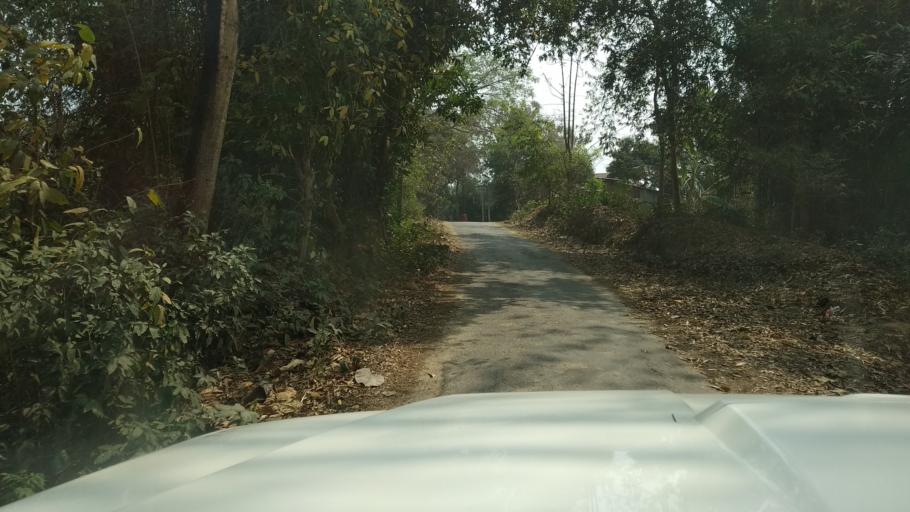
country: IN
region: Tripura
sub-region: West Tripura
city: Sonamura
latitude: 23.4285
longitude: 91.3150
